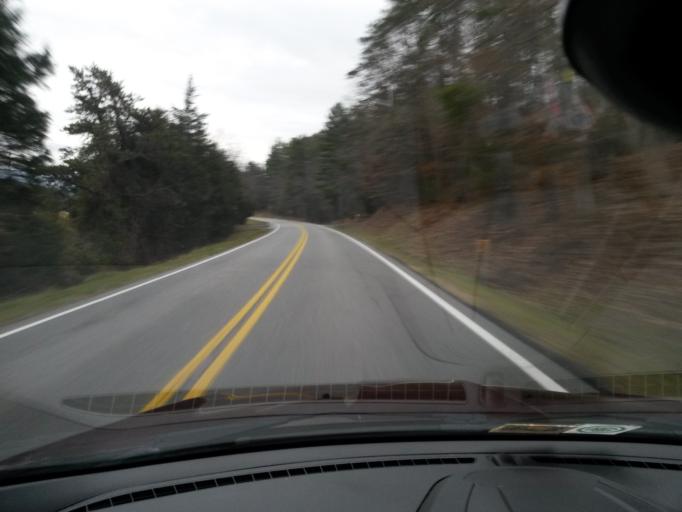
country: US
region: Virginia
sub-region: Bath County
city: Warm Springs
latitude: 38.0274
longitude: -79.6495
